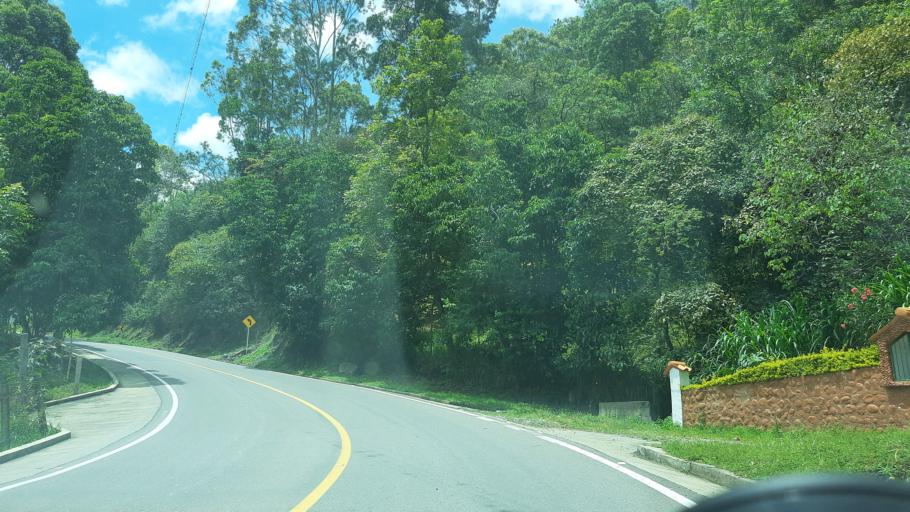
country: CO
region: Boyaca
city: Guateque
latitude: 5.0120
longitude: -73.4593
